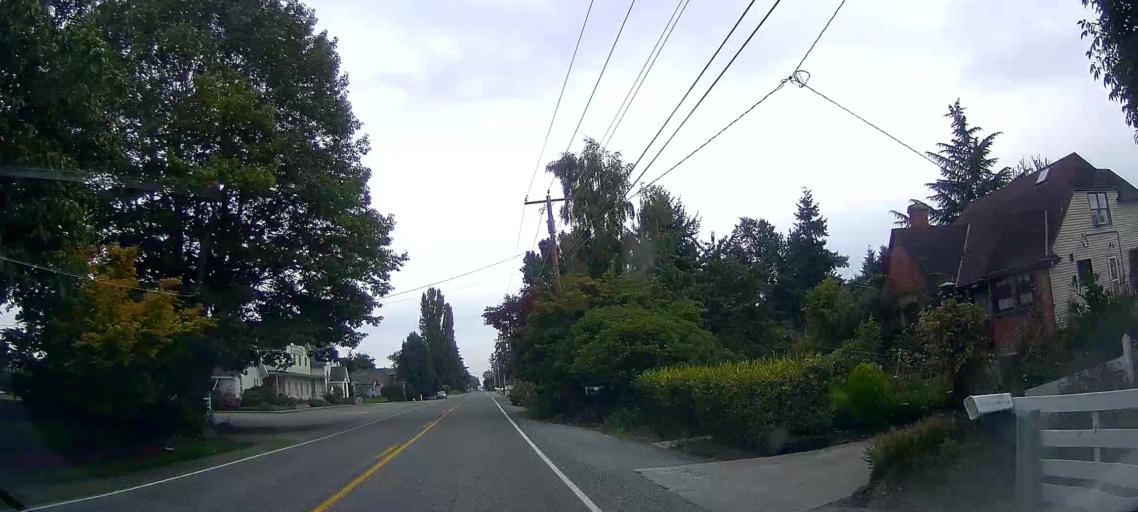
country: US
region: Washington
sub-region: Skagit County
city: Mount Vernon
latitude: 48.4468
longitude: -122.3786
